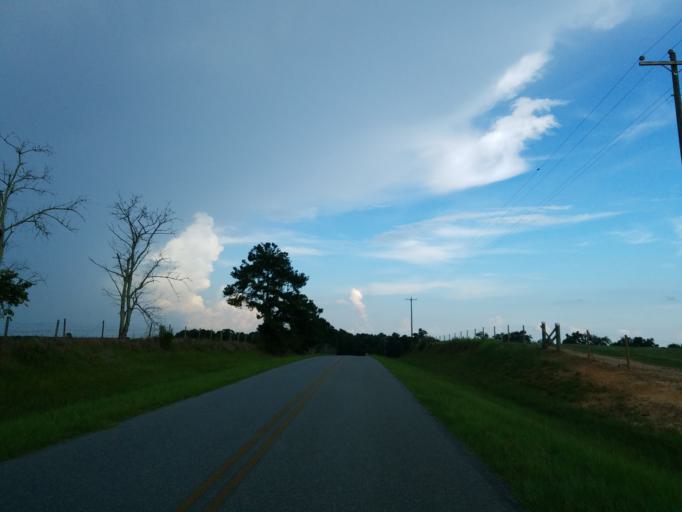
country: US
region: Georgia
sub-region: Tift County
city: Omega
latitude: 31.2659
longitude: -83.5168
